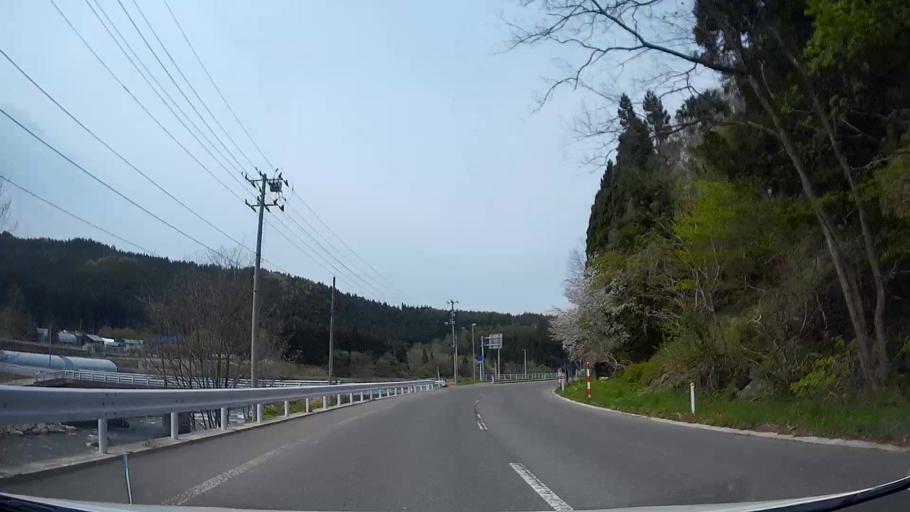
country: JP
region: Akita
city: Hanawa
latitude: 40.0764
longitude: 140.7932
